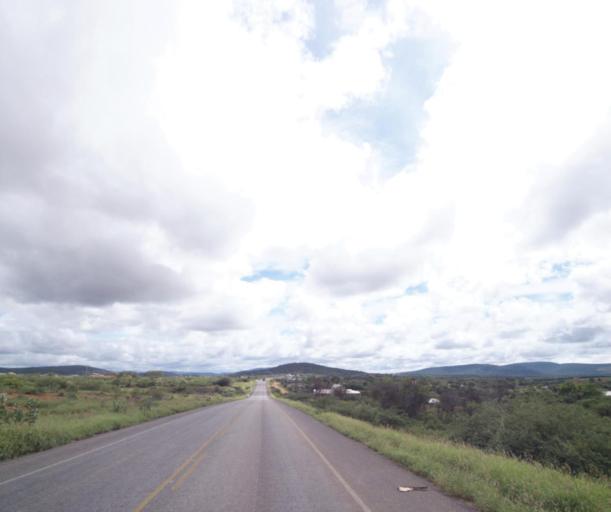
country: BR
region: Bahia
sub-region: Brumado
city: Brumado
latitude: -14.2268
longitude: -41.6750
